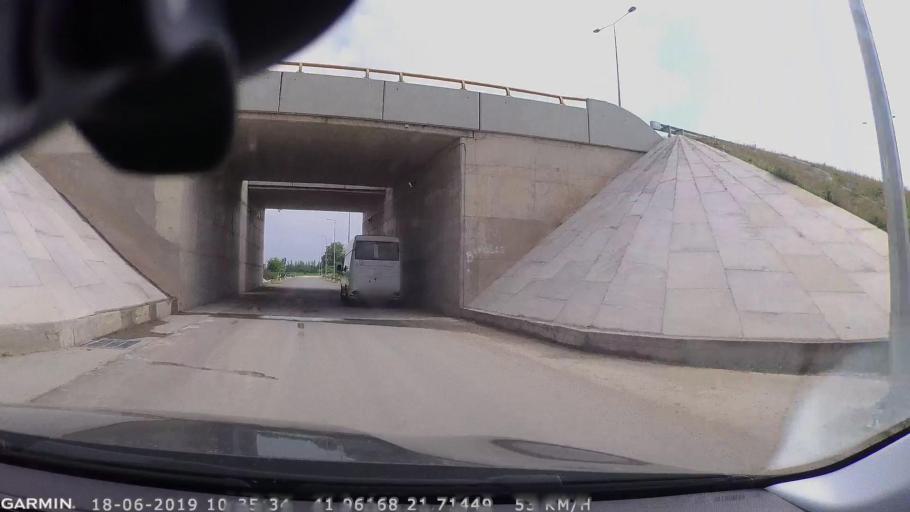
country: MK
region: Veles
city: Ivankovci
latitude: 41.9425
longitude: 21.8097
